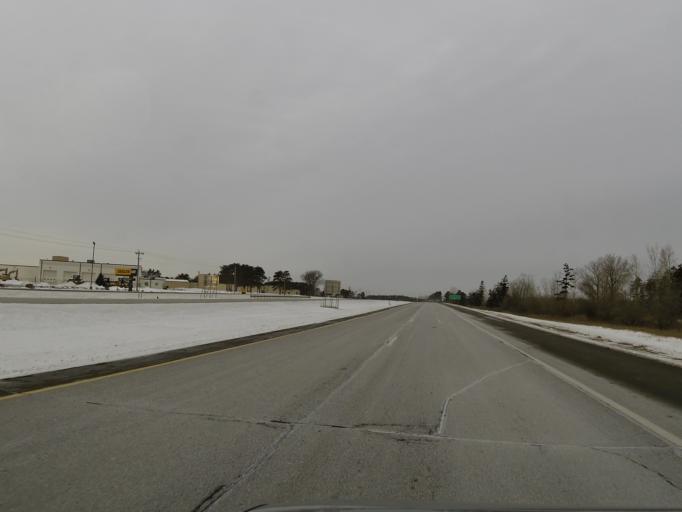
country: US
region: Minnesota
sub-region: Scott County
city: Savage
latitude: 44.7920
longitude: -93.4128
